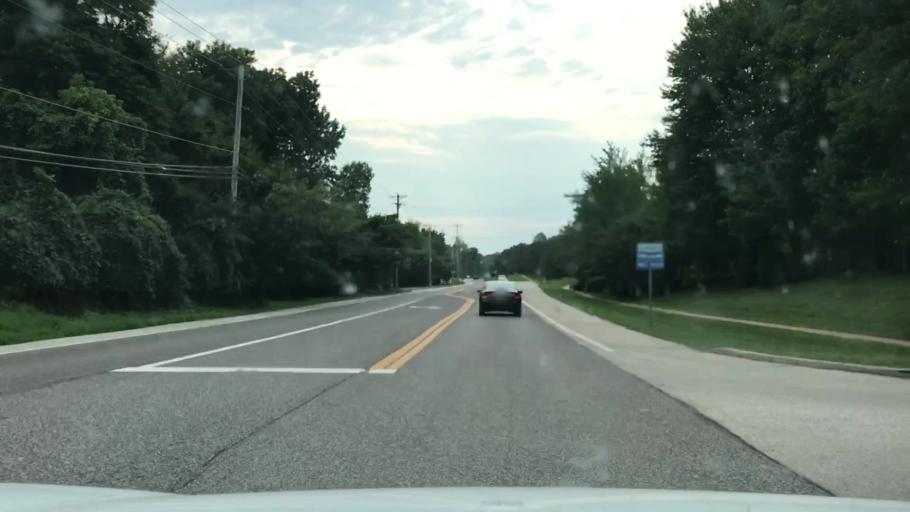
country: US
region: Missouri
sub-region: Saint Louis County
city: Chesterfield
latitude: 38.6559
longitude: -90.6099
